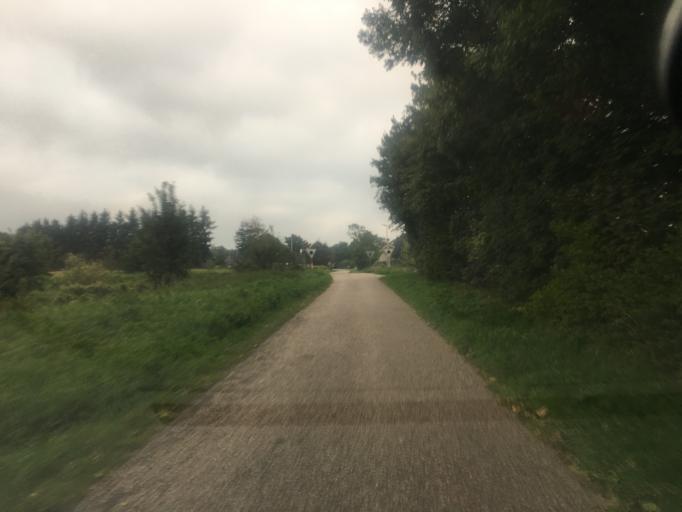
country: DE
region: Schleswig-Holstein
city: Ellhoft
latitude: 54.9420
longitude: 8.9592
